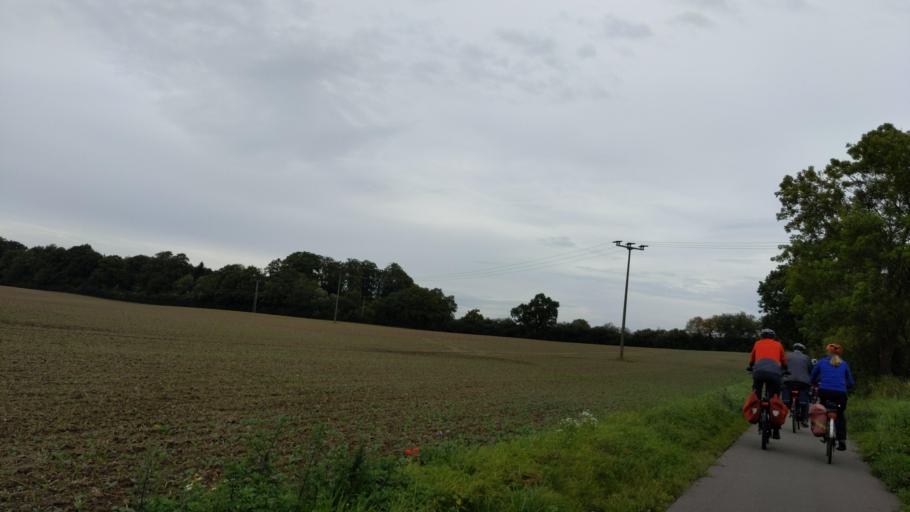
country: DE
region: Mecklenburg-Vorpommern
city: Schlagsdorf
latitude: 53.7511
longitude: 10.8271
